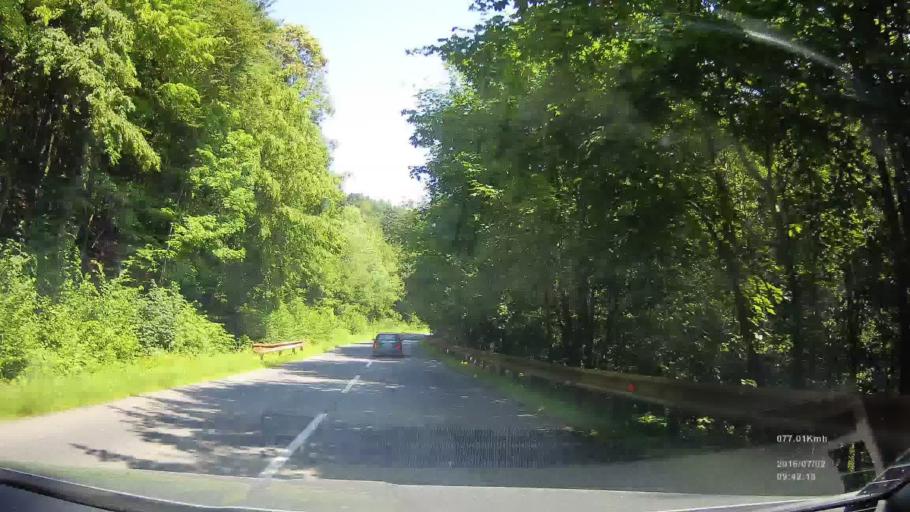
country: SK
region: Kosicky
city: Gelnica
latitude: 48.8402
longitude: 21.0365
